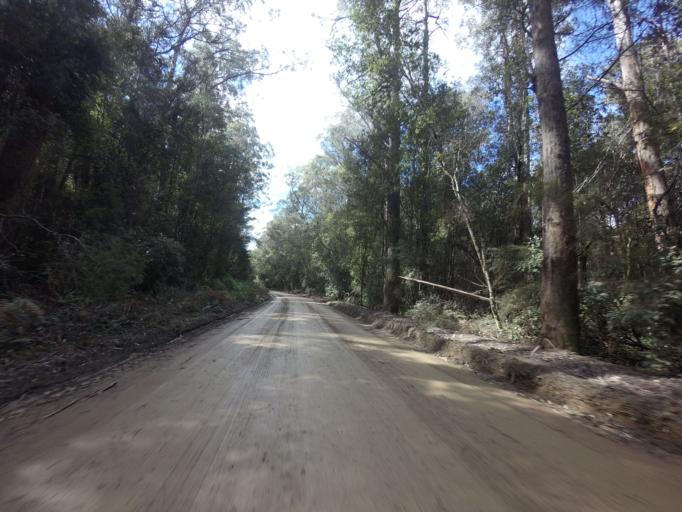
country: AU
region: Tasmania
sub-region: Huon Valley
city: Geeveston
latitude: -43.4163
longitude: 146.8883
